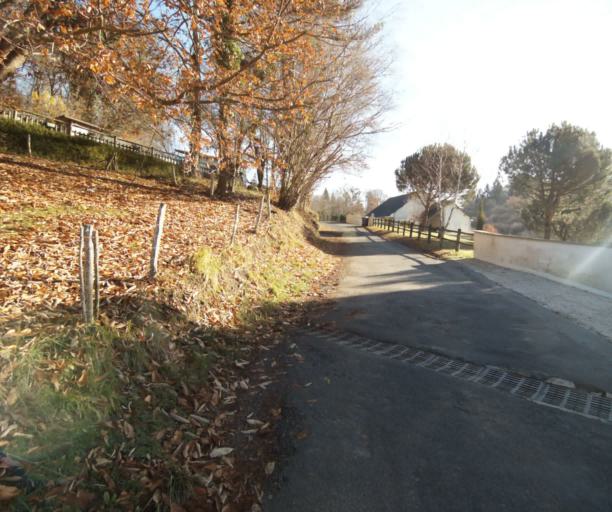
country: FR
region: Limousin
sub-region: Departement de la Correze
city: Chameyrat
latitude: 45.2358
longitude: 1.7375
